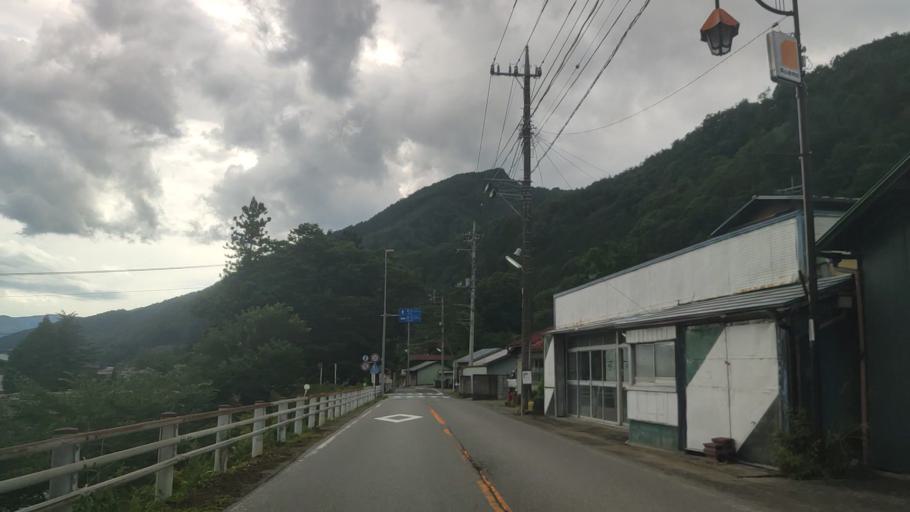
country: JP
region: Tochigi
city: Nikko
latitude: 36.6402
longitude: 139.4476
